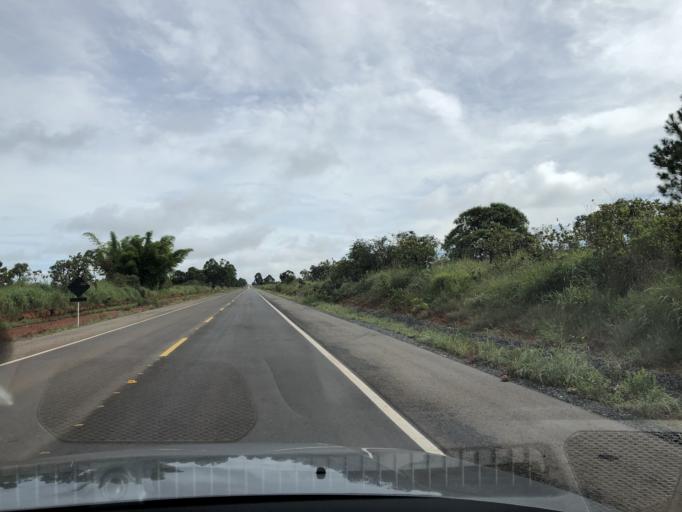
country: BR
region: Federal District
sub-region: Brasilia
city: Brasilia
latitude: -15.6616
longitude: -48.0851
